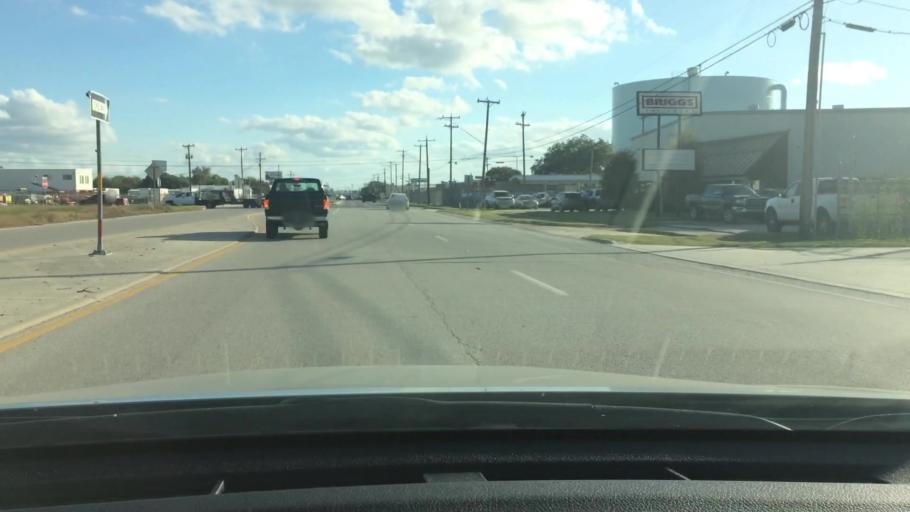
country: US
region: Texas
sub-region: Bexar County
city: Kirby
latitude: 29.4466
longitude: -98.4049
